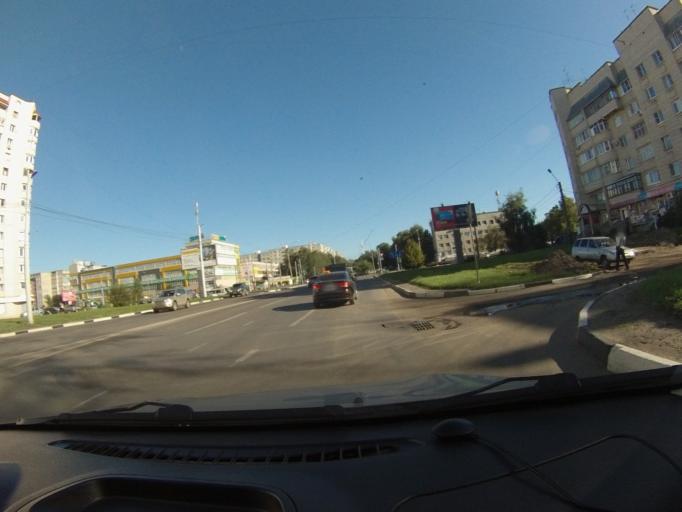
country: RU
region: Tambov
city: Tambov
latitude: 52.7569
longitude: 41.4301
